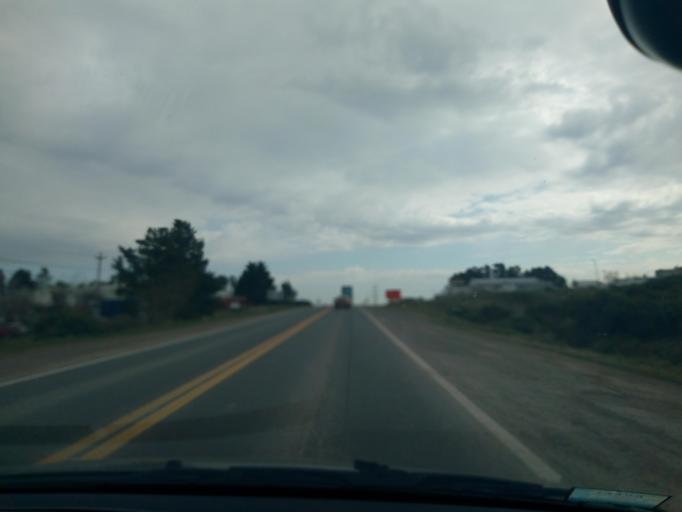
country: AR
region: Buenos Aires
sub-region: Partido de Tandil
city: Tandil
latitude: -37.3243
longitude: -59.0976
